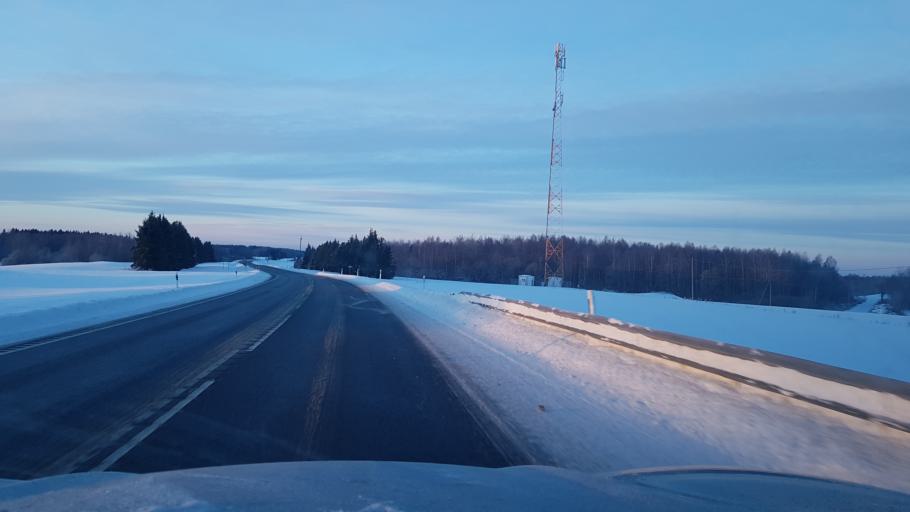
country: EE
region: Ida-Virumaa
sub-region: Narva-Joesuu linn
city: Narva-Joesuu
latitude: 59.3891
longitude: 27.9783
